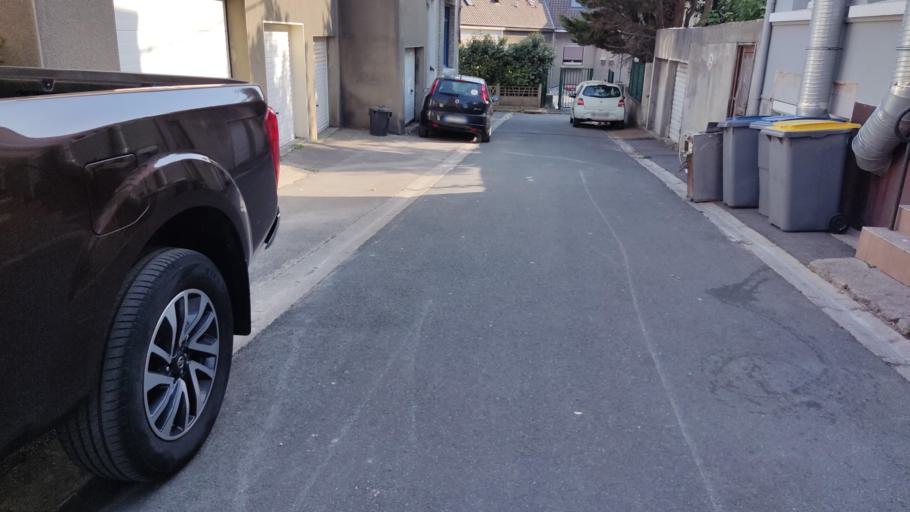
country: FR
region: Nord-Pas-de-Calais
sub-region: Departement du Pas-de-Calais
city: Le Portel
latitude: 50.7062
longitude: 1.5744
